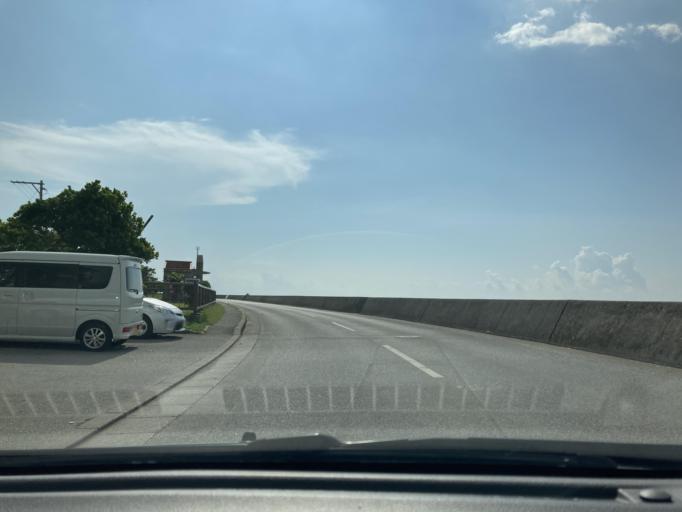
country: JP
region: Okinawa
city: Itoman
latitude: 26.1278
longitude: 127.7715
